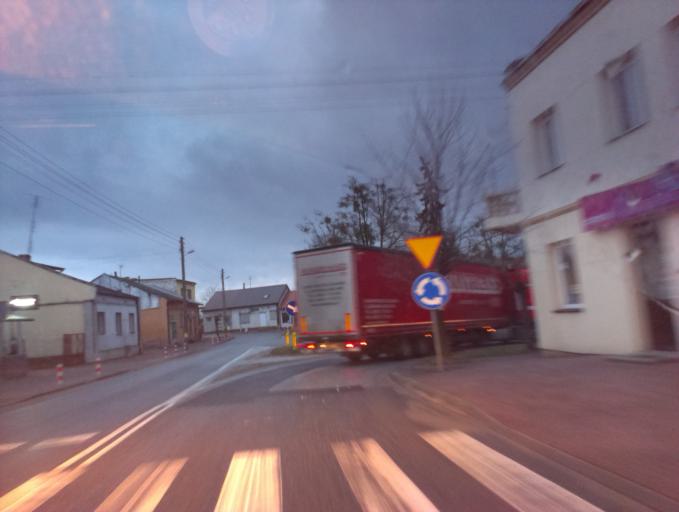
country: PL
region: Lodz Voivodeship
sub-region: Powiat opoczynski
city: Zarnow
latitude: 51.2468
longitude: 20.1722
